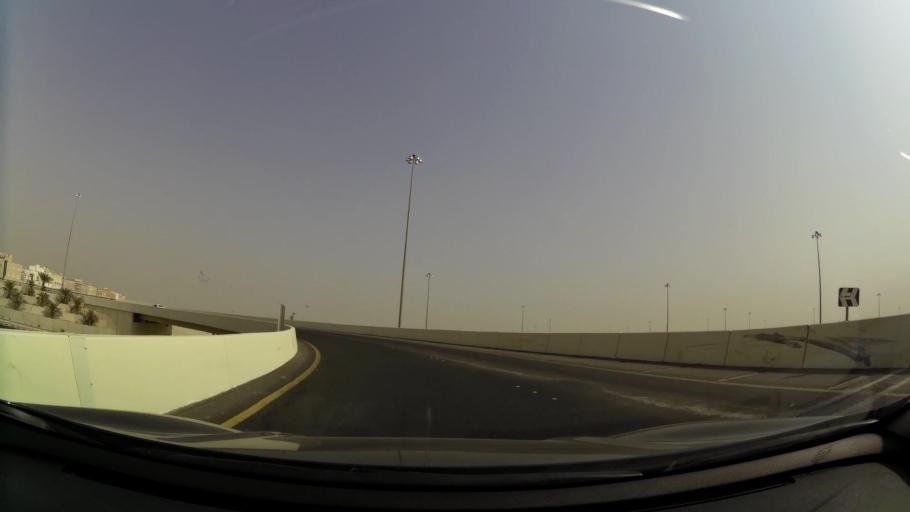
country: KW
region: Muhafazat al Jahra'
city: Al Jahra'
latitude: 29.2961
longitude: 47.7302
